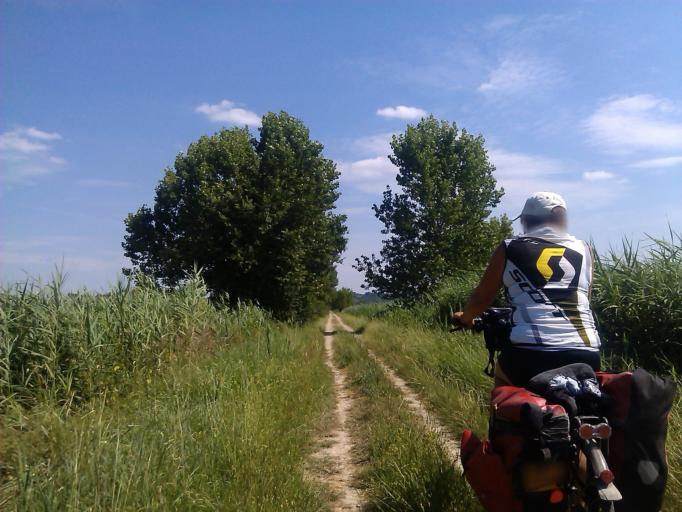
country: IT
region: Tuscany
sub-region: Provincia di Siena
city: Chiusi
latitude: 43.0668
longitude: 11.9296
